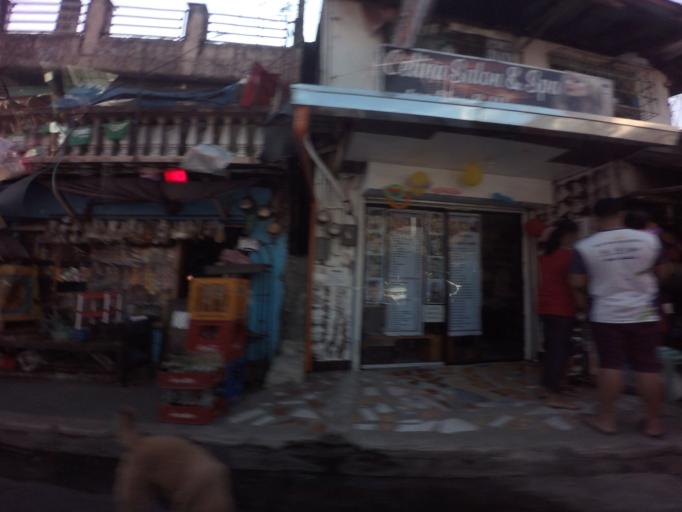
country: PH
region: Calabarzon
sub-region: Province of Rizal
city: Taguig
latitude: 14.4917
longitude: 121.0476
